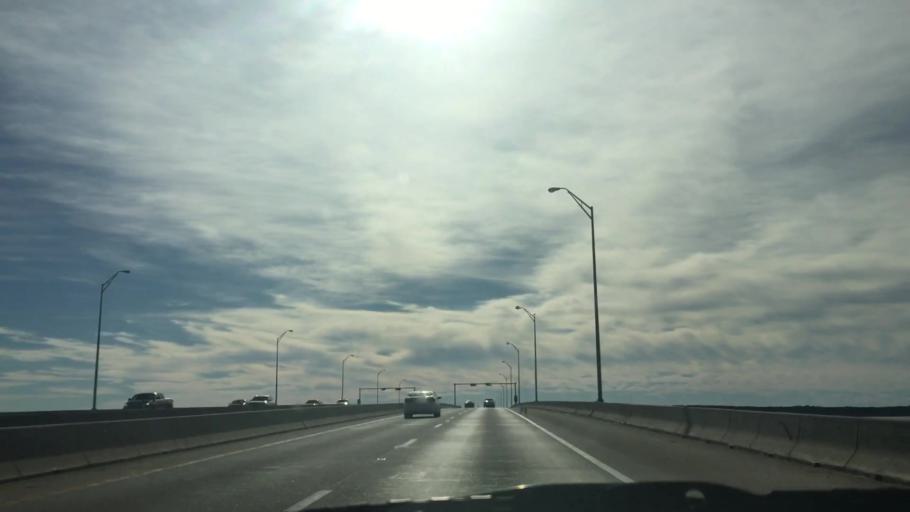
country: US
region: Virginia
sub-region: City of Newport News
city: Newport News
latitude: 36.9128
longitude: -76.4076
